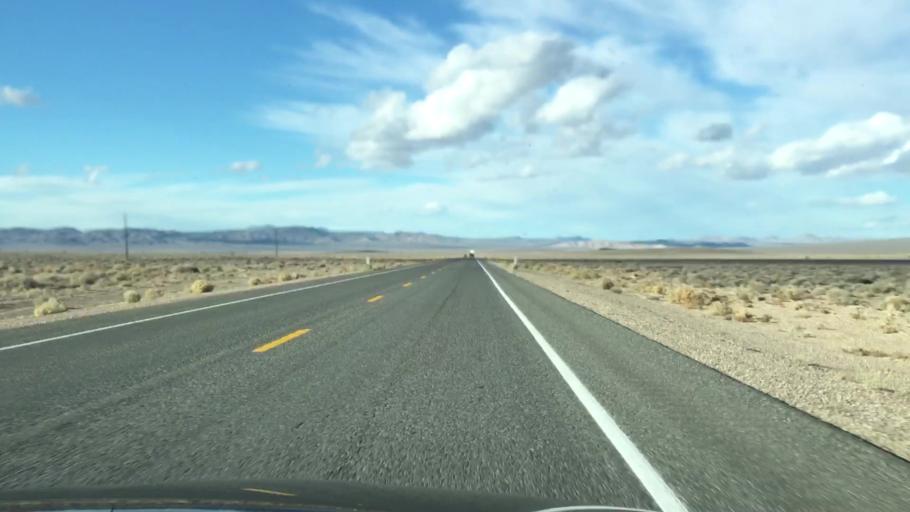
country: US
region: Nevada
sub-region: Esmeralda County
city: Goldfield
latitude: 37.3978
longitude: -117.1477
